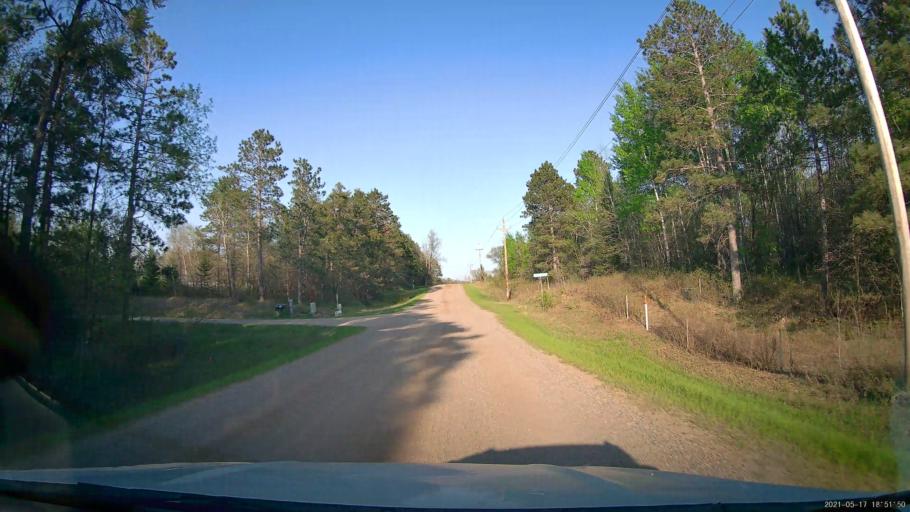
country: US
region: Minnesota
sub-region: Hubbard County
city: Park Rapids
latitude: 46.9438
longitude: -95.0074
